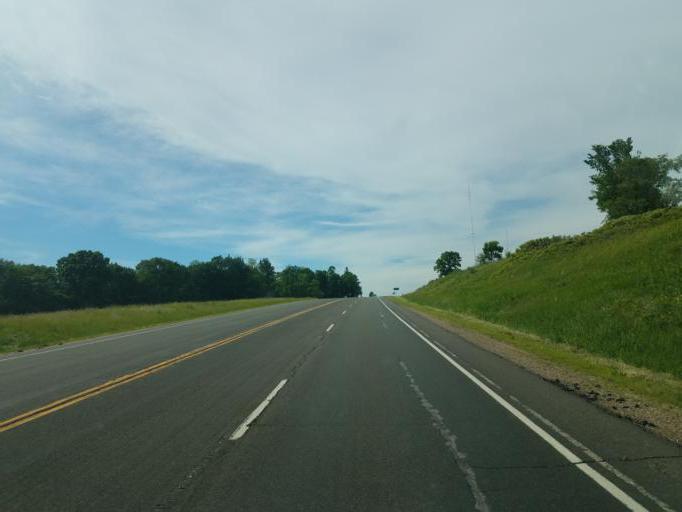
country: US
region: Wisconsin
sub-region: Monroe County
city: Tomah
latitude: 43.8950
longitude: -90.4880
